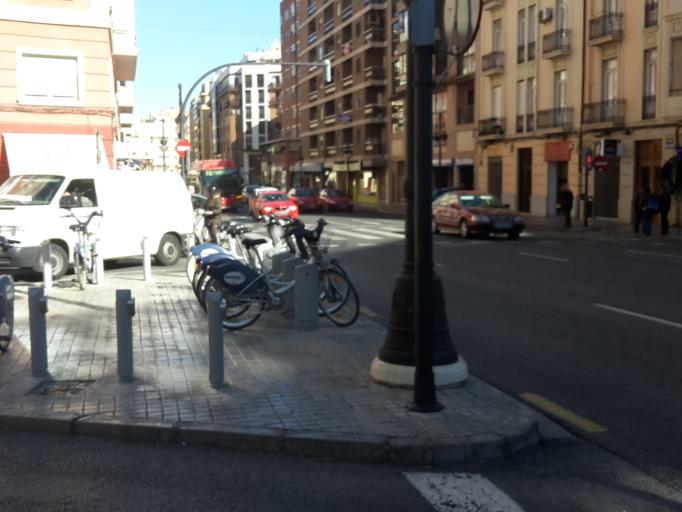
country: ES
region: Valencia
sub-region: Provincia de Valencia
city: Valencia
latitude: 39.4697
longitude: -0.3886
